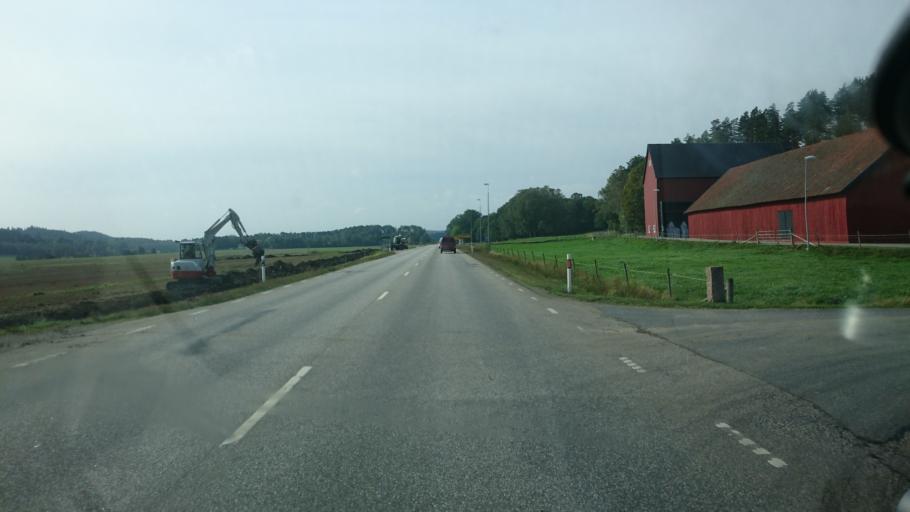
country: SE
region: Vaestra Goetaland
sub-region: Alingsas Kommun
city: Sollebrunn
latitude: 58.1112
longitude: 12.5253
